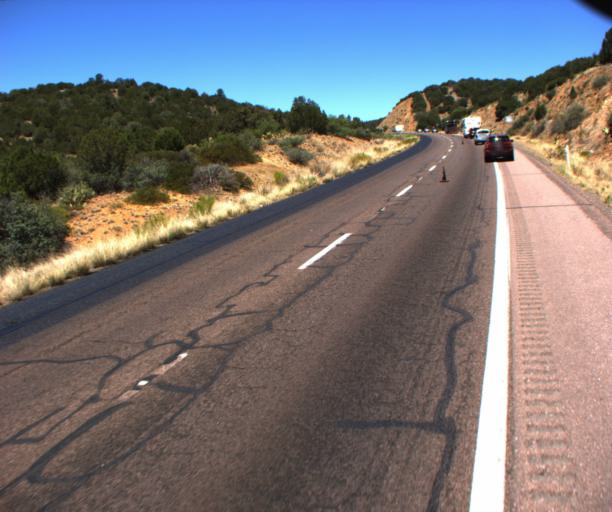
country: US
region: Arizona
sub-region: Gila County
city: Payson
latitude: 34.1632
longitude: -111.3253
